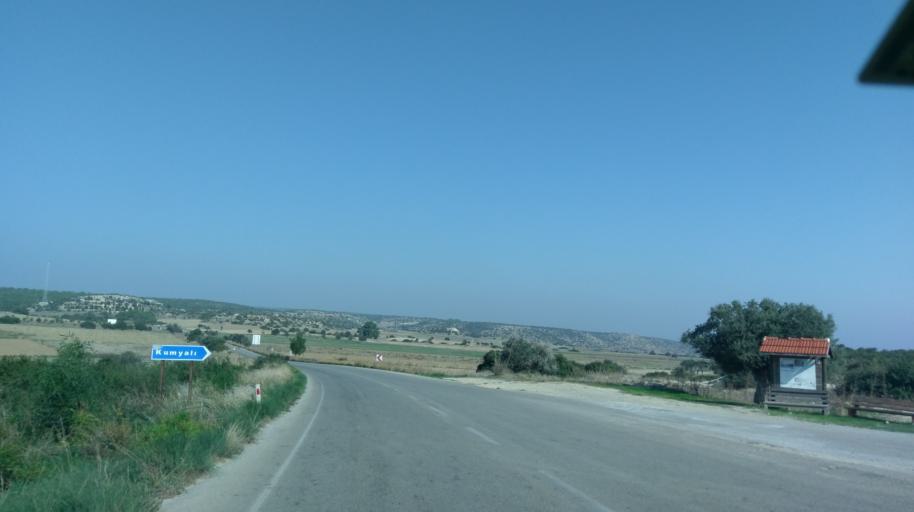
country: CY
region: Ammochostos
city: Leonarisso
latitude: 35.4347
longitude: 34.1338
